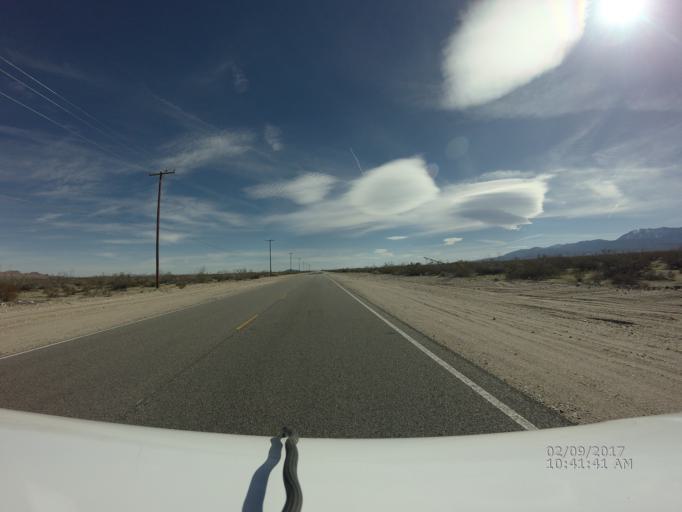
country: US
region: California
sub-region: Los Angeles County
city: Littlerock
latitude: 34.5428
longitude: -117.9016
